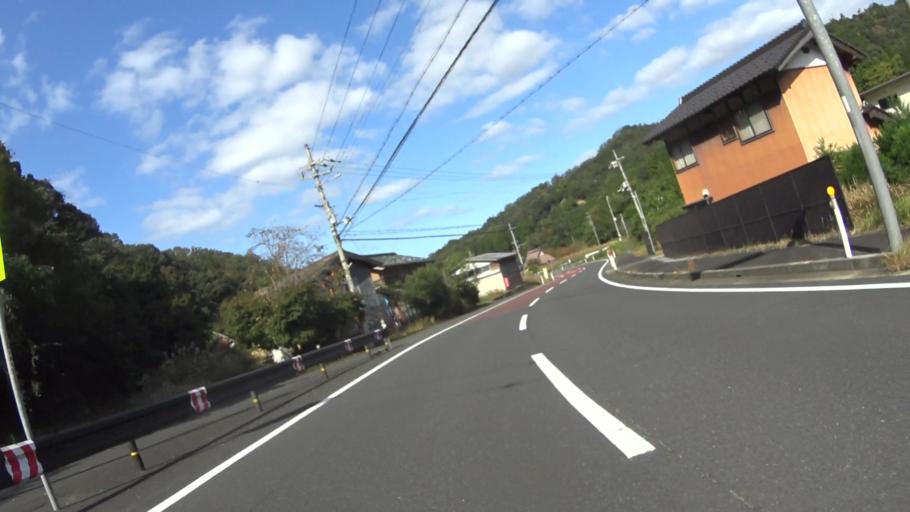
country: JP
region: Hyogo
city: Toyooka
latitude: 35.5610
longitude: 134.9788
